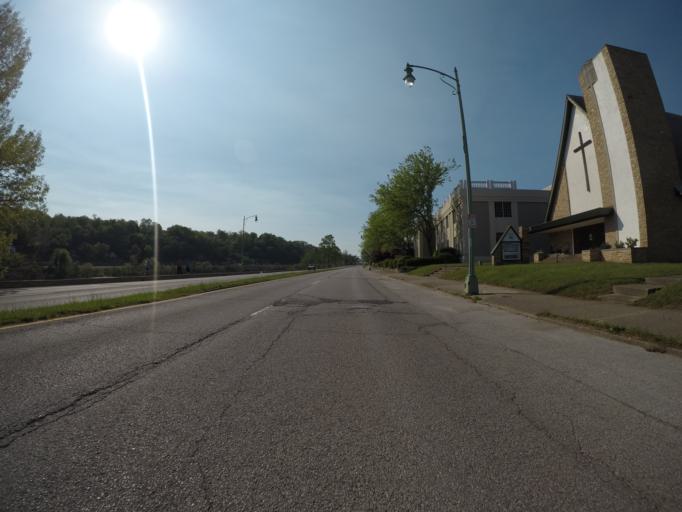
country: US
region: West Virginia
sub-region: Kanawha County
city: Charleston
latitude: 38.3410
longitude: -81.6272
